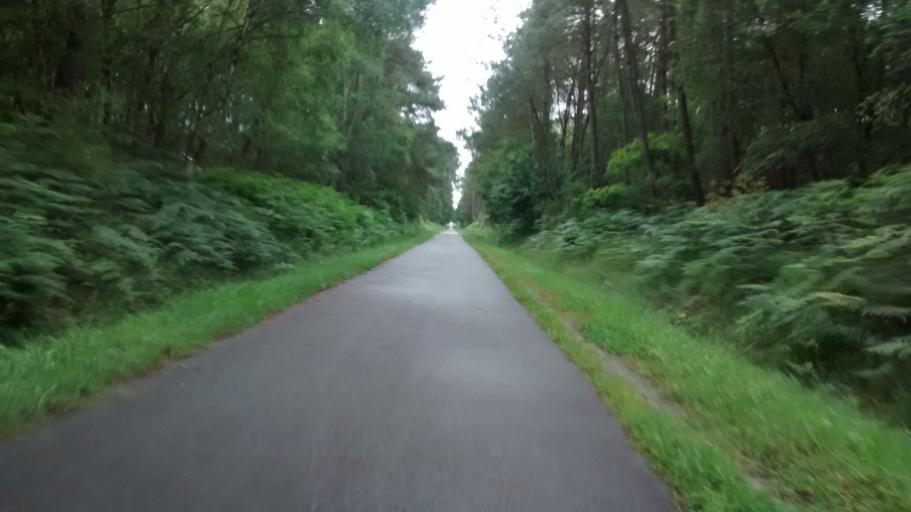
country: FR
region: Brittany
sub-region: Departement du Morbihan
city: Molac
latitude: 47.7381
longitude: -2.4120
